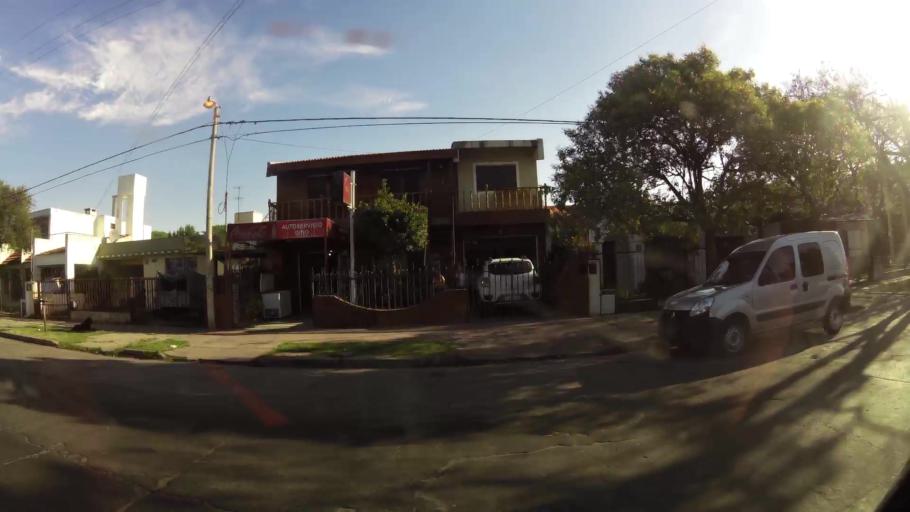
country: AR
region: Cordoba
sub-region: Departamento de Capital
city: Cordoba
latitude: -31.3597
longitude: -64.2211
